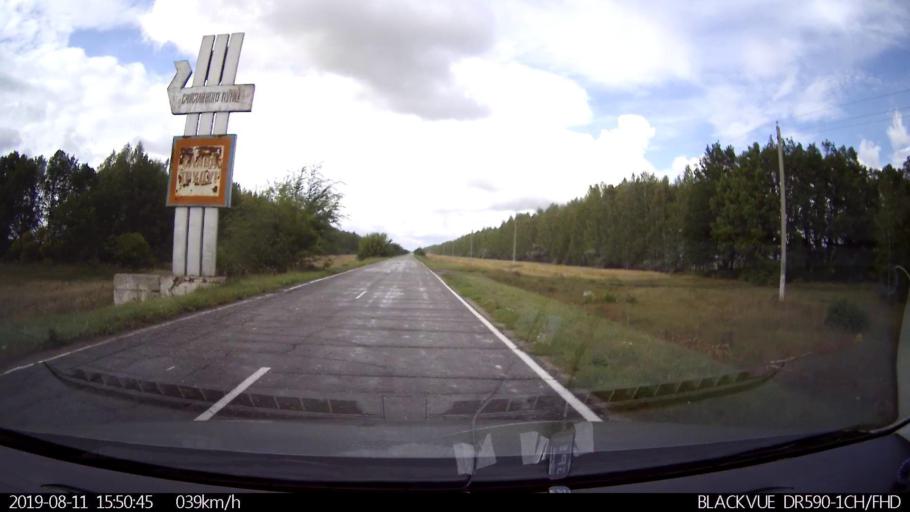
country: RU
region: Ulyanovsk
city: Ignatovka
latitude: 53.9139
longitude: 47.6559
